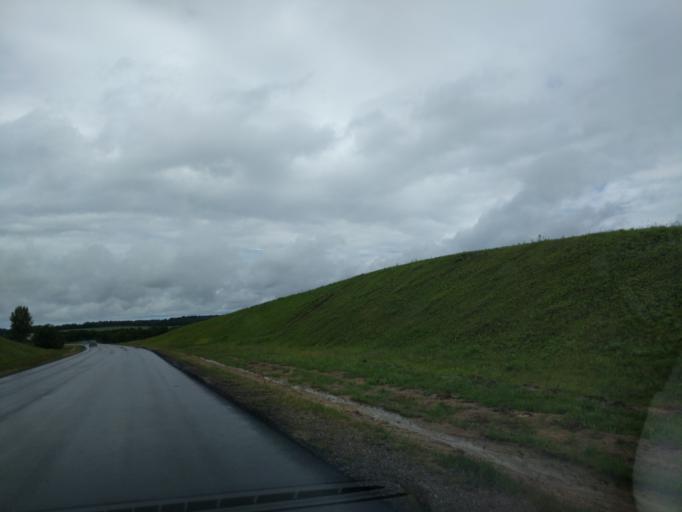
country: BY
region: Minsk
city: Il'ya
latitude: 54.2905
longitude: 27.4851
